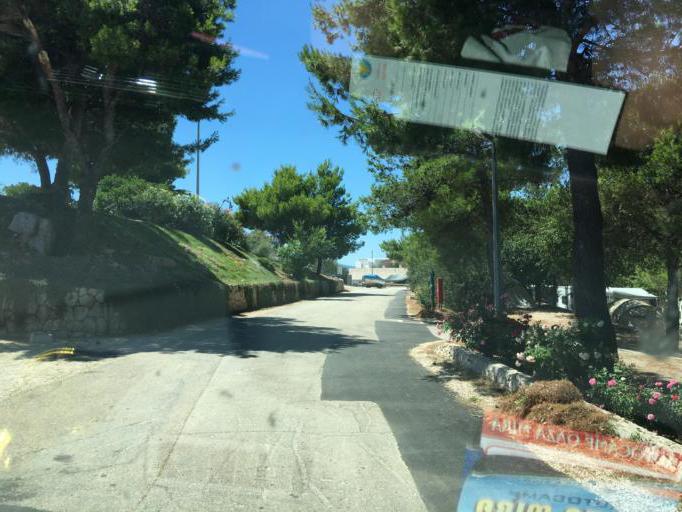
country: HR
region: Zadarska
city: Pakostane
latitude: 43.8860
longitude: 15.5326
